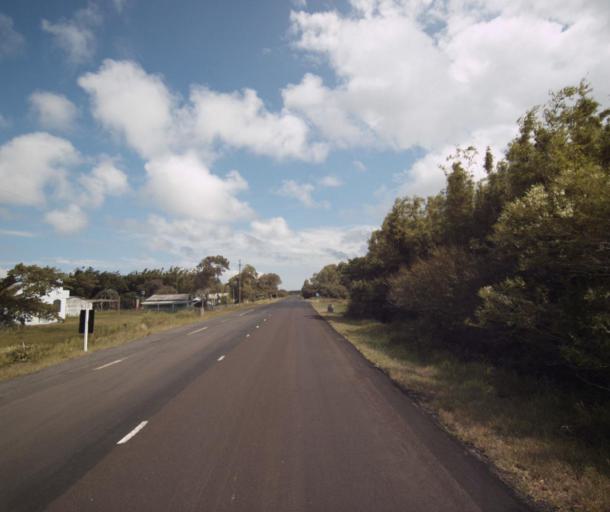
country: BR
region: Rio Grande do Sul
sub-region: Tapes
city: Tapes
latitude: -31.4046
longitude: -51.1657
